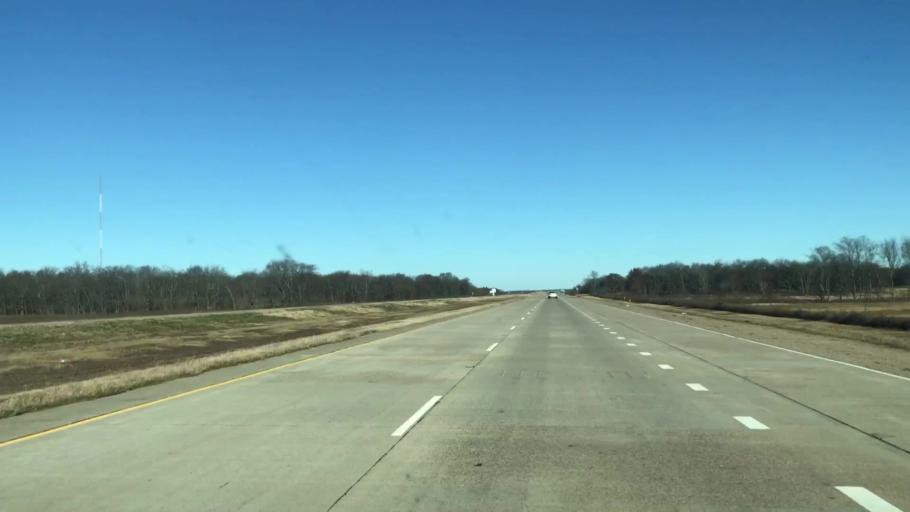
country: US
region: Louisiana
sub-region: Caddo Parish
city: Blanchard
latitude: 32.6804
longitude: -93.8523
